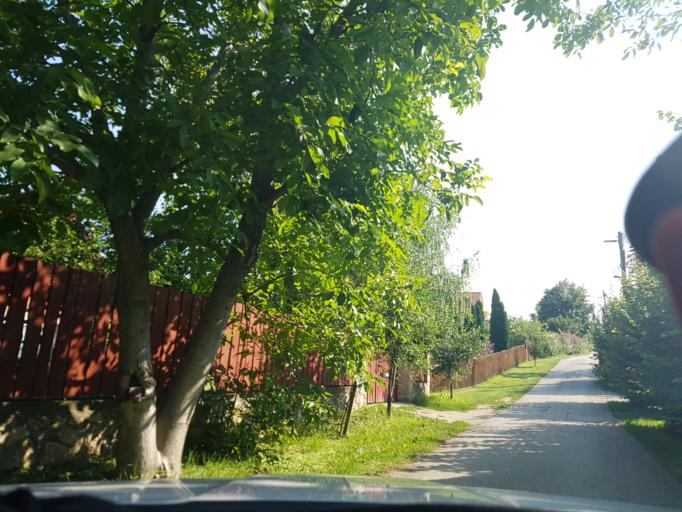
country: HU
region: Veszprem
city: Csopak
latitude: 46.9928
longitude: 17.9766
